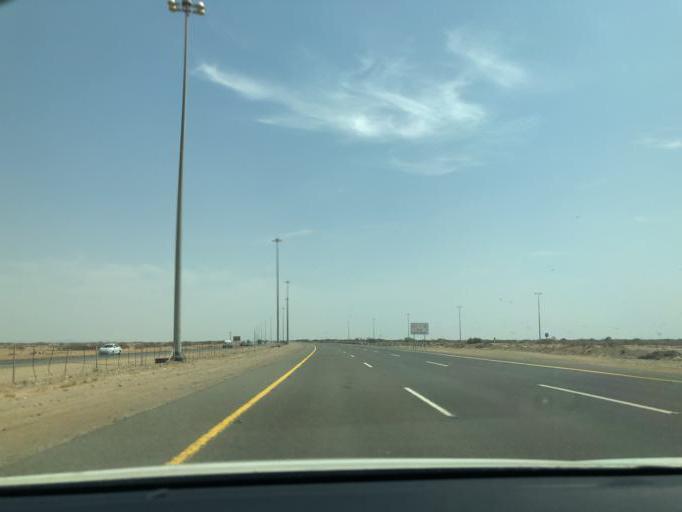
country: SA
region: Makkah
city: Rabigh
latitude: 22.2412
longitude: 39.1136
